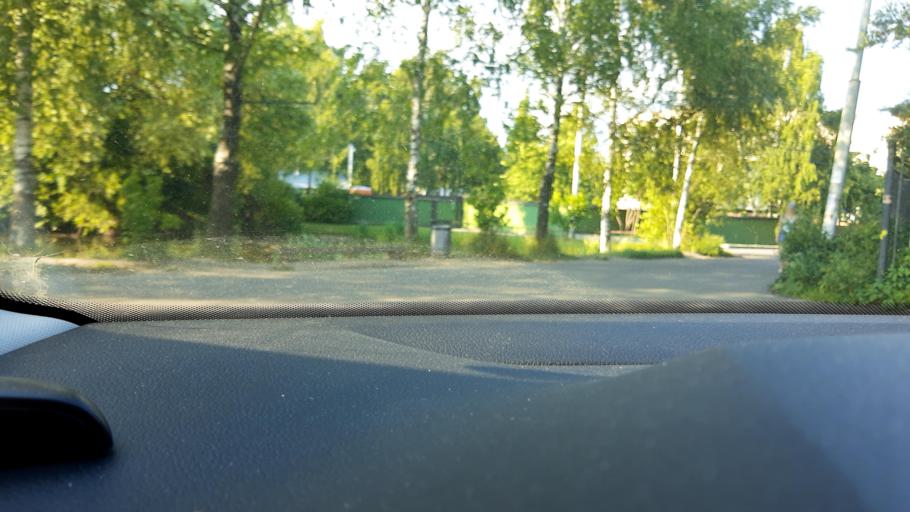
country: RU
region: Moskovskaya
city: Novopodrezkovo
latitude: 55.8989
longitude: 37.3748
